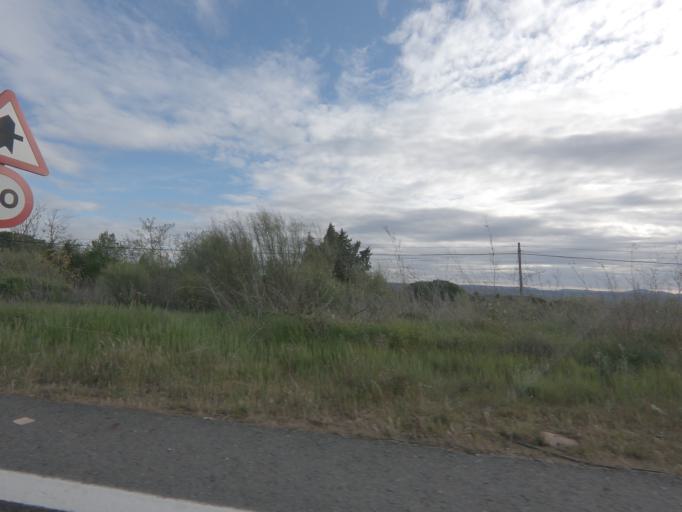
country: ES
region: Extremadura
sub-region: Provincia de Caceres
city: Coria
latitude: 40.0063
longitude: -6.5575
